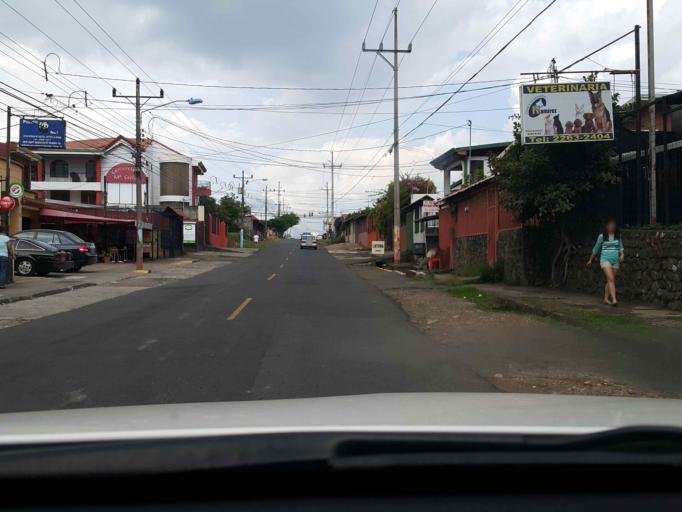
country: CR
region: Heredia
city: San Rafael
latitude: 10.0124
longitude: -84.0982
